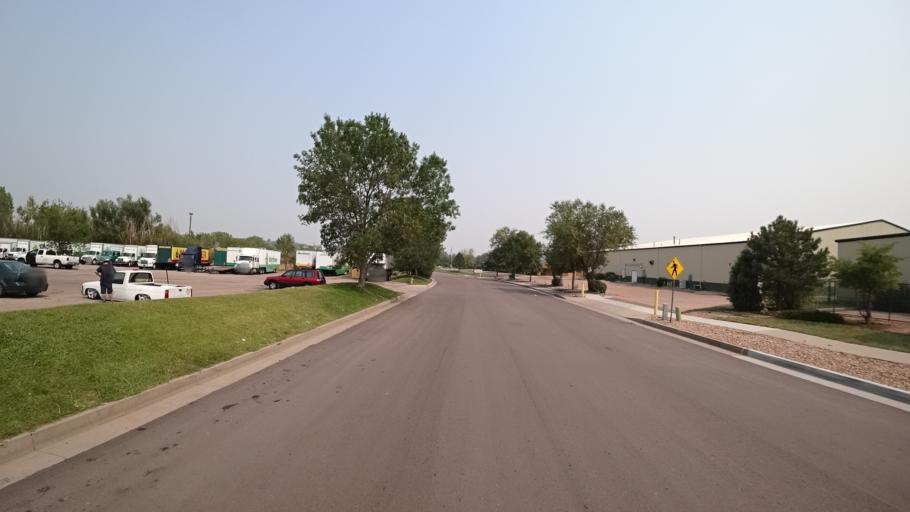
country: US
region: Colorado
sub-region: El Paso County
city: Stratmoor
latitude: 38.7897
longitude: -104.7888
